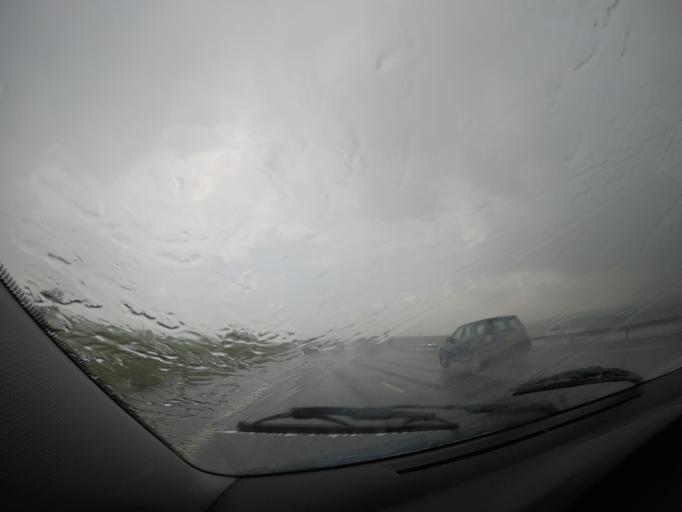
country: GB
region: England
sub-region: Cumbria
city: Penrith
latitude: 54.7075
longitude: -2.7931
